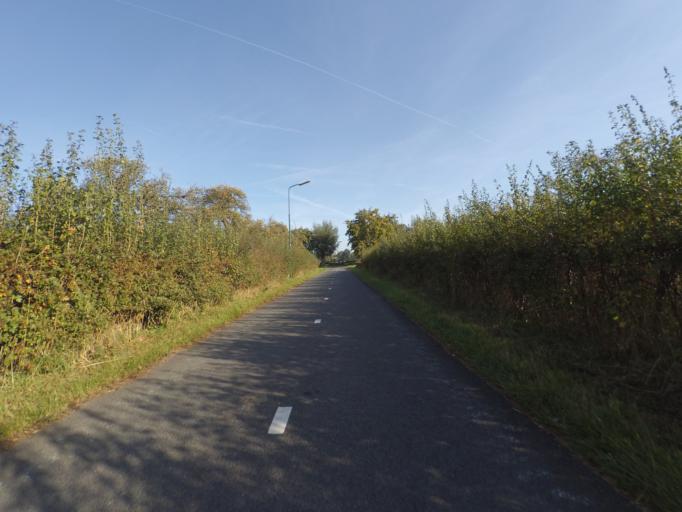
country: NL
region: Utrecht
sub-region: Gemeente De Bilt
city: De Bilt
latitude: 52.0965
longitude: 5.1785
